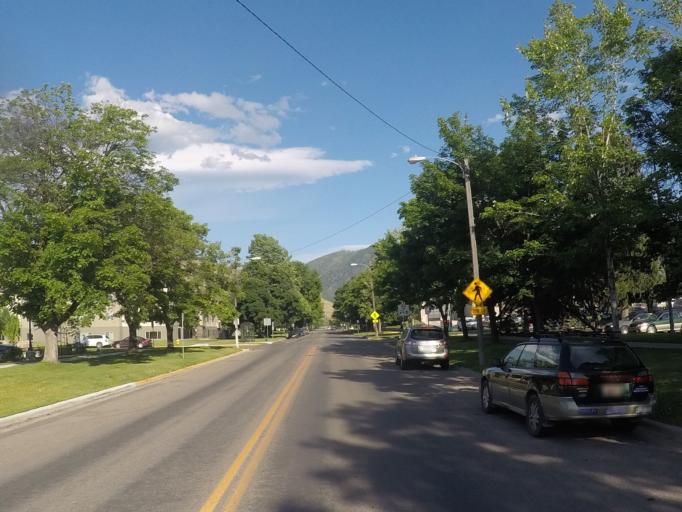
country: US
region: Montana
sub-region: Missoula County
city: Missoula
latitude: 46.8766
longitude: -114.0014
